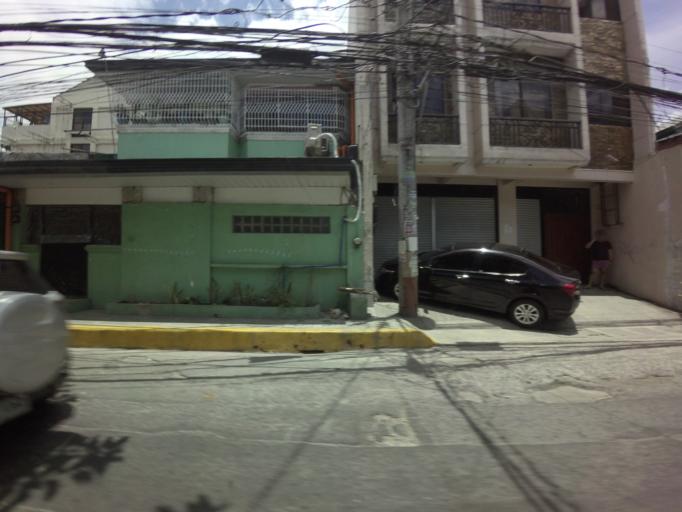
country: PH
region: Metro Manila
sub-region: Marikina
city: Calumpang
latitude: 14.6039
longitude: 121.1031
